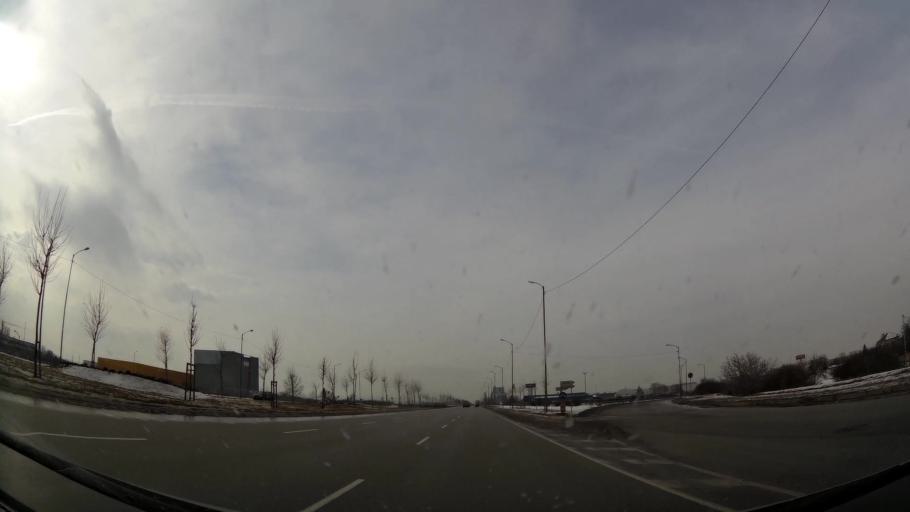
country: BG
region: Sofia-Capital
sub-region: Stolichna Obshtina
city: Sofia
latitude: 42.7066
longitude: 23.4045
